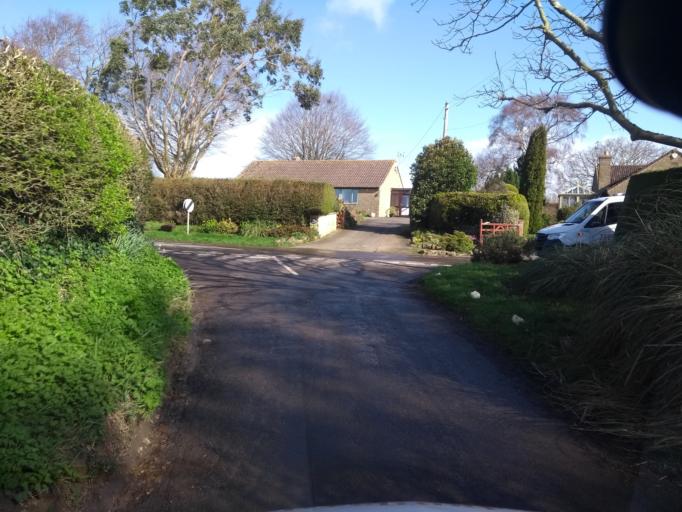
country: GB
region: England
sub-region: Somerset
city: South Petherton
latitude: 50.9678
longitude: -2.8336
